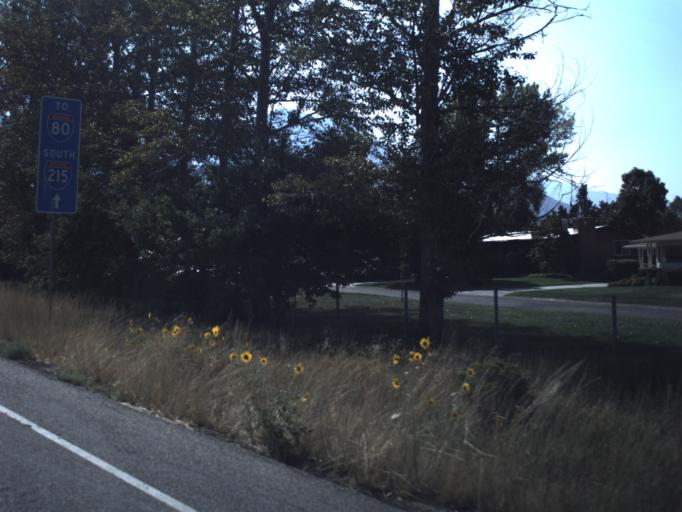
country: US
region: Utah
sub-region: Salt Lake County
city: Canyon Rim
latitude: 40.7174
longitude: -111.8117
